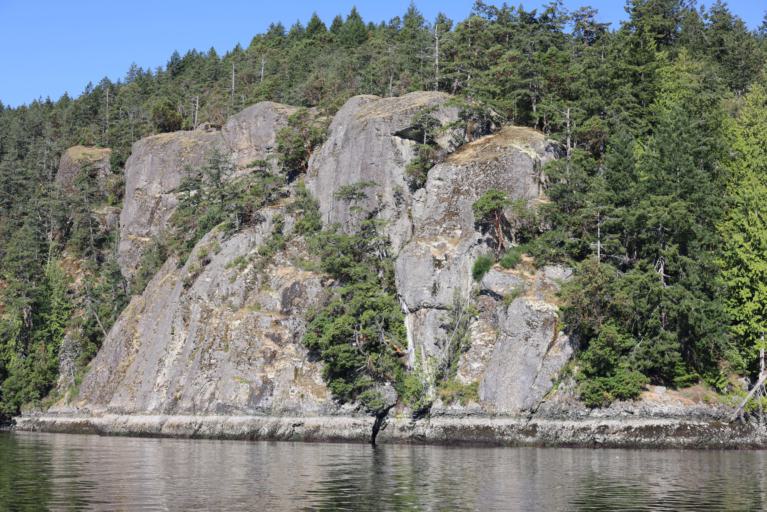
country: CA
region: British Columbia
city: North Cowichan
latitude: 48.7950
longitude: -123.5610
